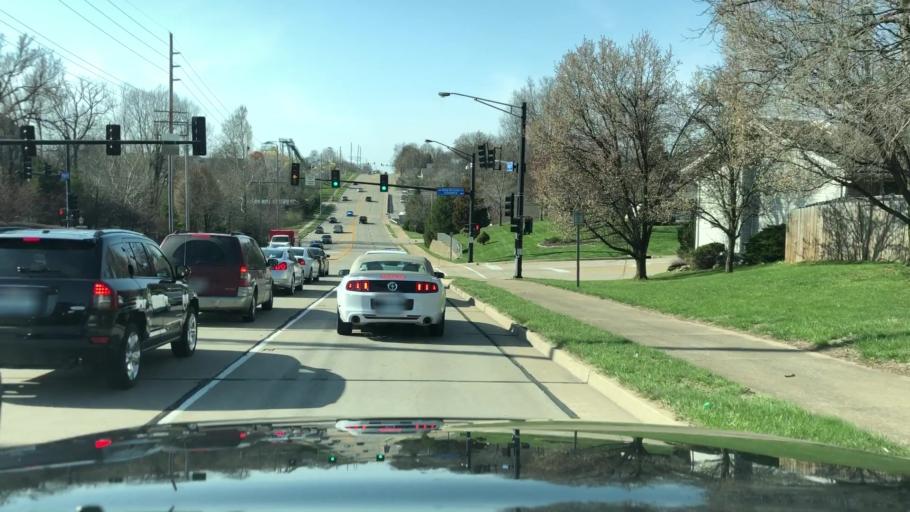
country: US
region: Missouri
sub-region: Saint Charles County
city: Saint Charles
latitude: 38.7646
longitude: -90.5433
